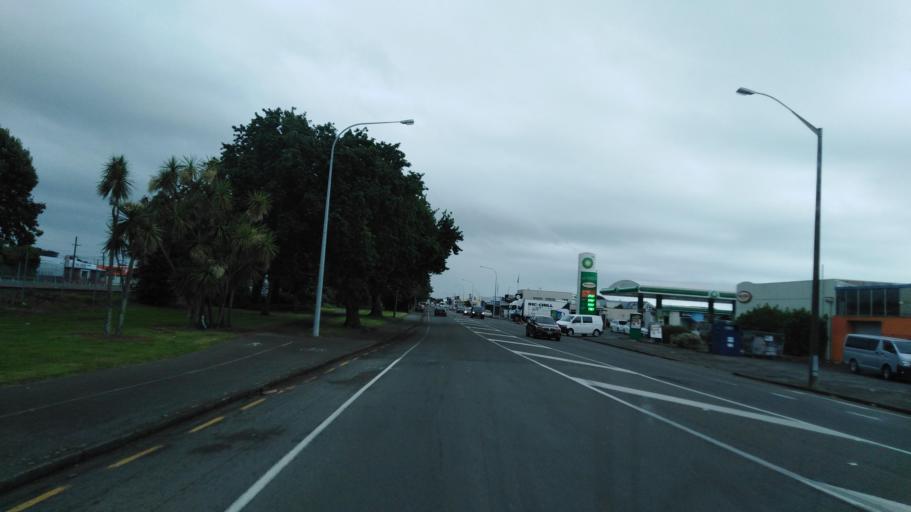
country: NZ
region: Manawatu-Wanganui
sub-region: Horowhenua District
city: Levin
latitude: -40.6292
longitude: 175.2796
